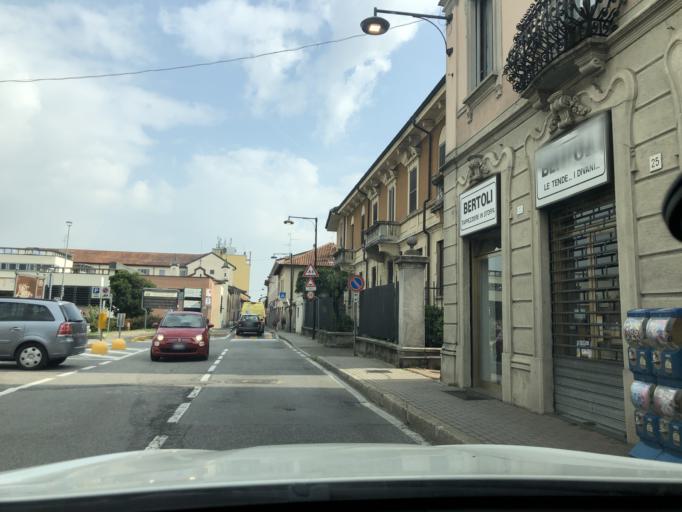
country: IT
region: Lombardy
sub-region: Citta metropolitana di Milano
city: Carugate
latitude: 45.5488
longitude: 9.3377
